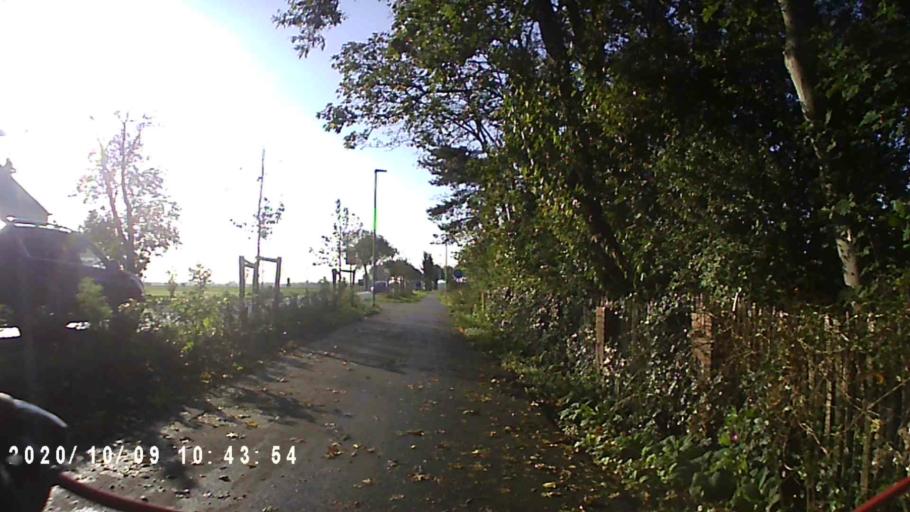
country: NL
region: Groningen
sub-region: Gemeente Groningen
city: Korrewegwijk
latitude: 53.2694
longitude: 6.5362
